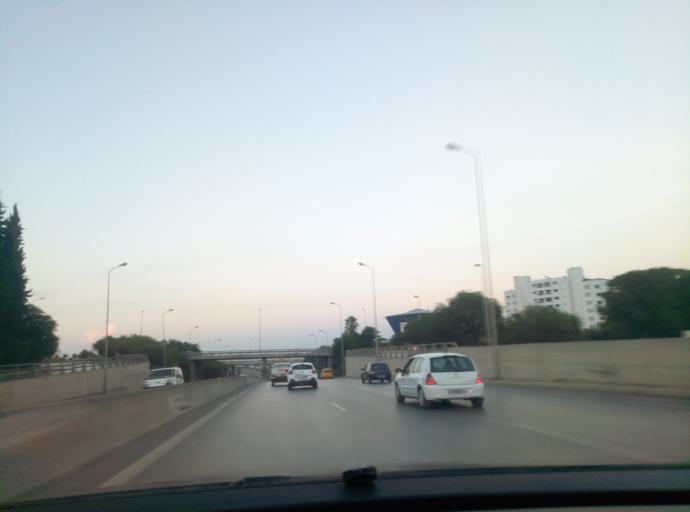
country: TN
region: Tunis
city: Tunis
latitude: 36.8324
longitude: 10.1543
